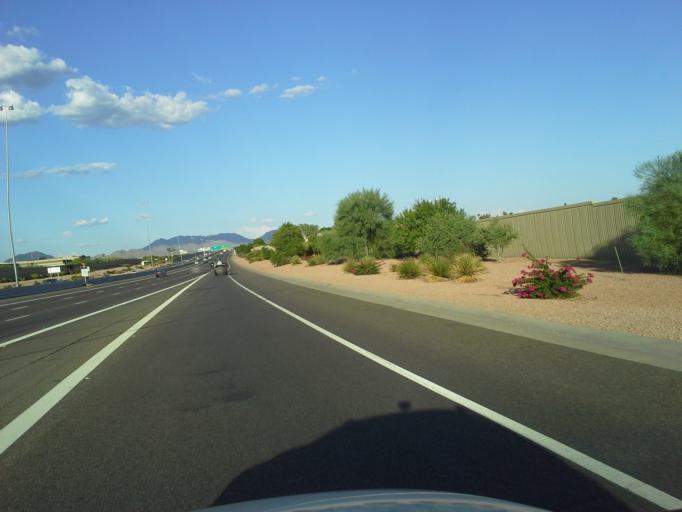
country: US
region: Arizona
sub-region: Maricopa County
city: Paradise Valley
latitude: 33.6725
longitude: -112.0262
